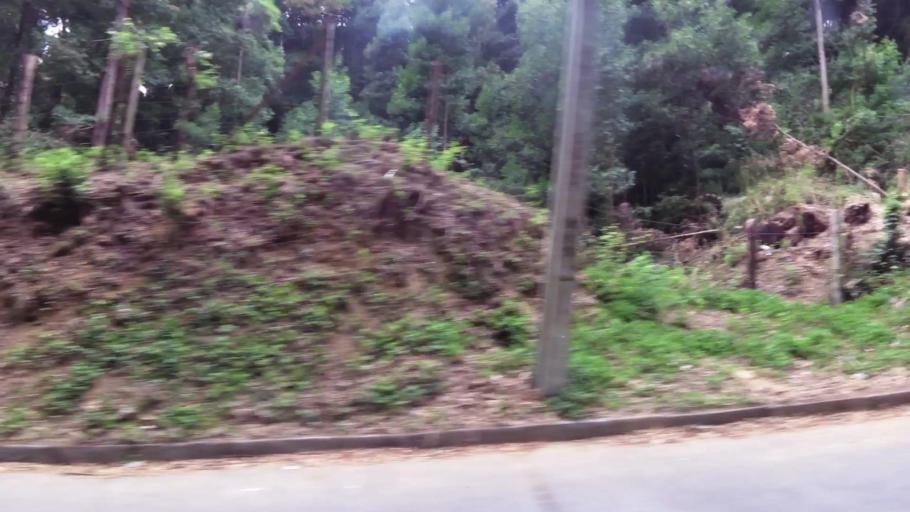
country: CL
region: Biobio
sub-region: Provincia de Concepcion
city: Concepcion
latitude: -36.8231
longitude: -73.0308
